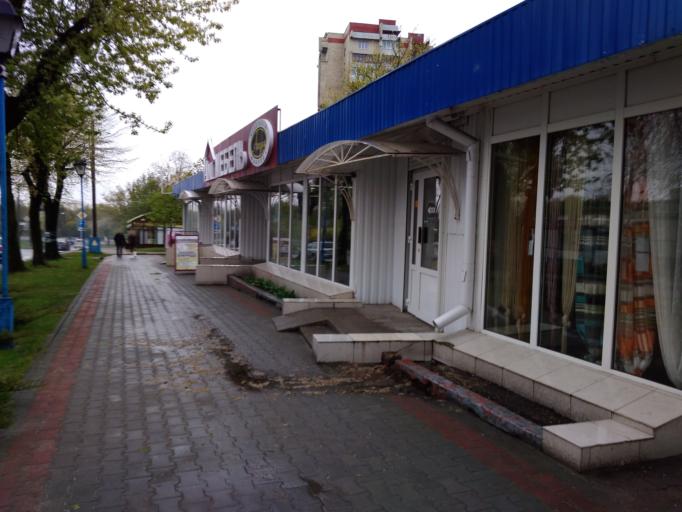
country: BY
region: Brest
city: Brest
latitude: 52.0844
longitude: 23.6942
